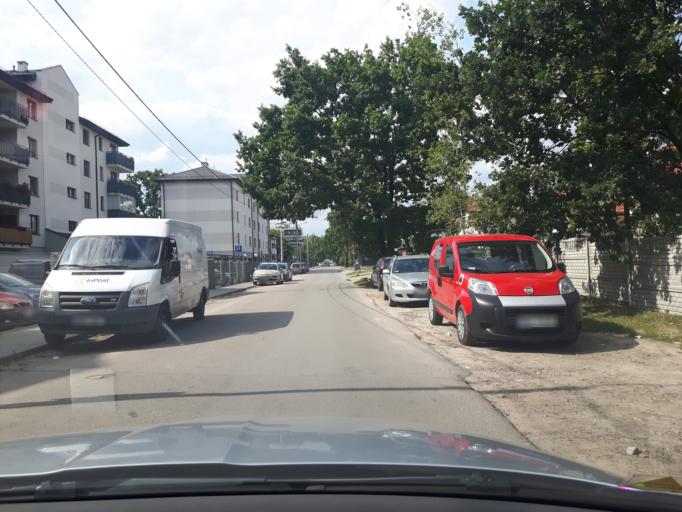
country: PL
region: Masovian Voivodeship
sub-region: Powiat wolominski
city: Marki
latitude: 52.3089
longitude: 21.1015
